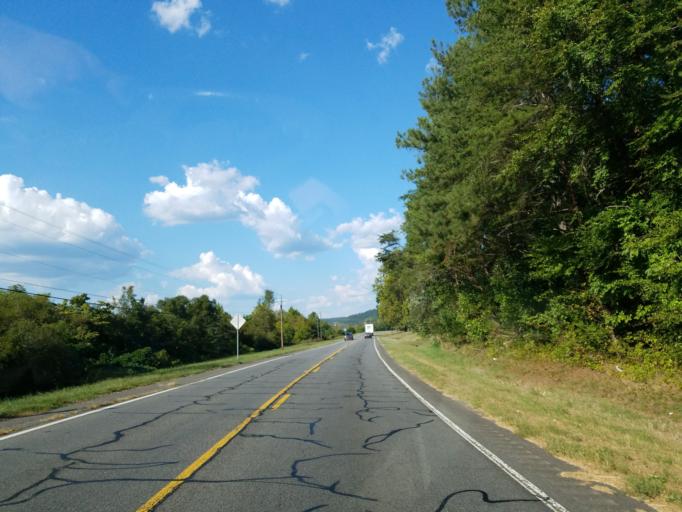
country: US
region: Georgia
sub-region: Bartow County
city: Rydal
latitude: 34.4001
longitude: -84.7089
